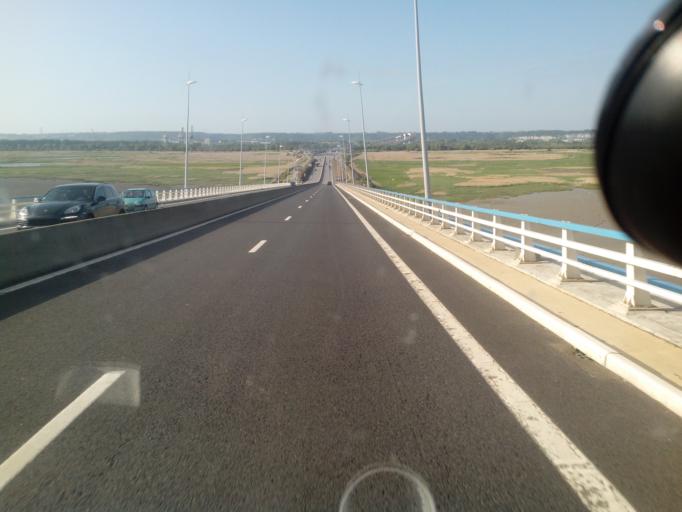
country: FR
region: Lower Normandy
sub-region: Departement du Calvados
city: La Riviere-Saint-Sauveur
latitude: 49.4398
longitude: 0.2731
